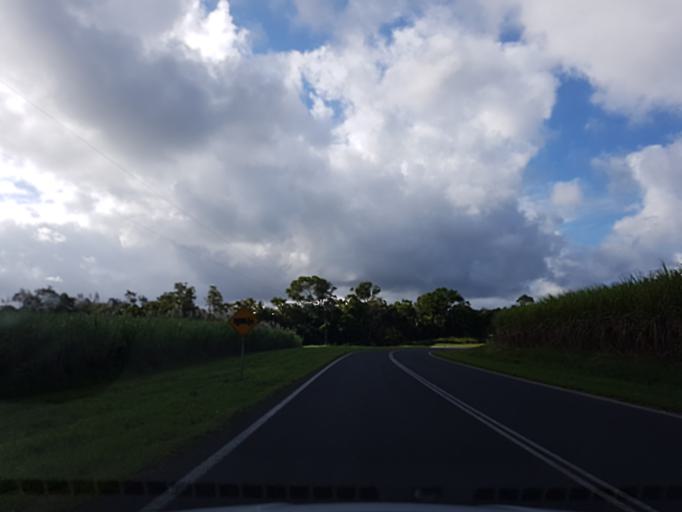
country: AU
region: Queensland
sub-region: Cairns
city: Port Douglas
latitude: -16.2803
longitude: 145.3797
